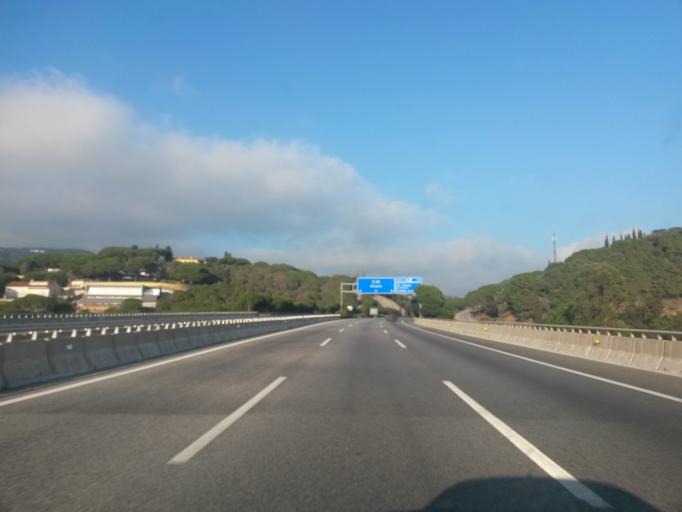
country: ES
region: Catalonia
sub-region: Provincia de Barcelona
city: Sant Andreu de Llavaneres
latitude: 41.5683
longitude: 2.4990
